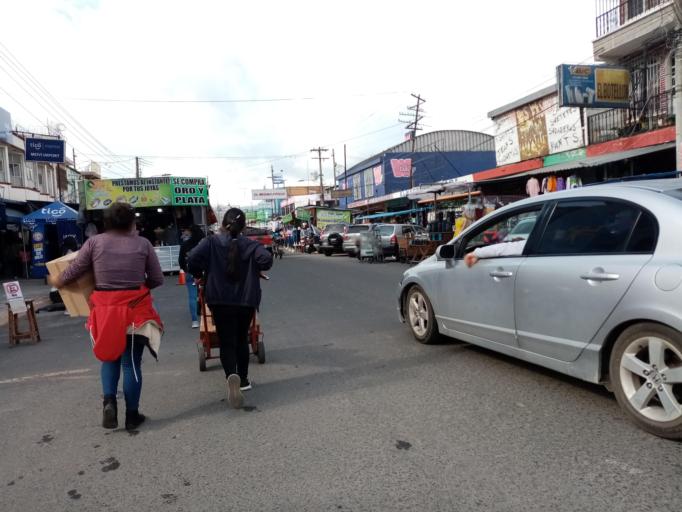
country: GT
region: Quetzaltenango
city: Quetzaltenango
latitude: 14.8409
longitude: -91.5198
